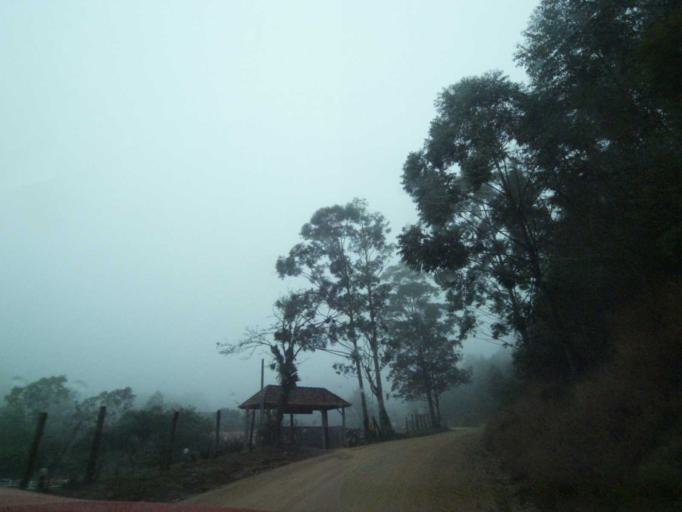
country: BR
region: Santa Catarina
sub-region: Anitapolis
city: Anitapolis
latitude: -27.9132
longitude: -49.1081
